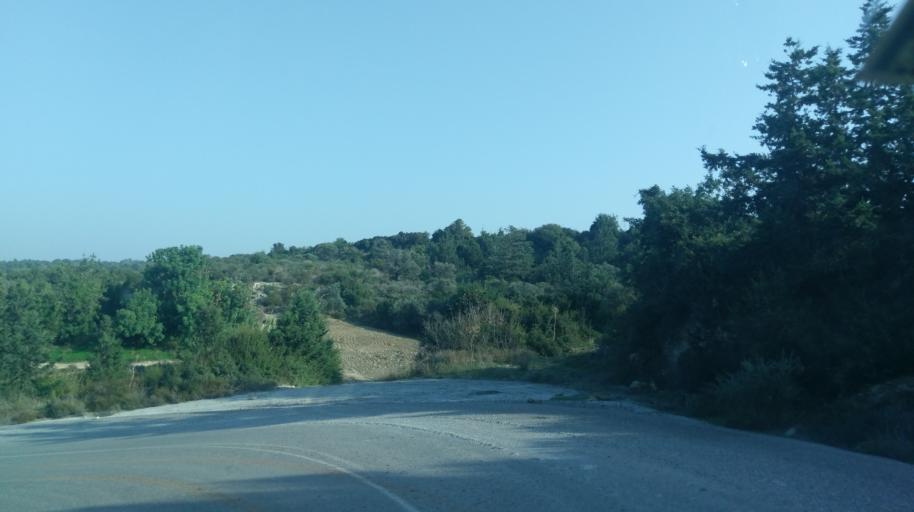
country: CY
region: Ammochostos
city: Leonarisso
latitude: 35.5500
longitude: 34.2281
